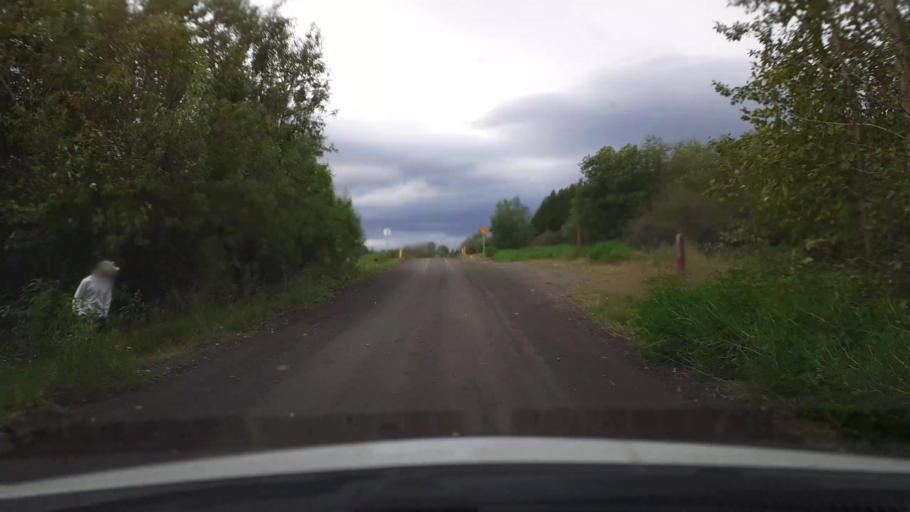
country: IS
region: Capital Region
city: Mosfellsbaer
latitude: 64.5213
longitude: -21.4587
